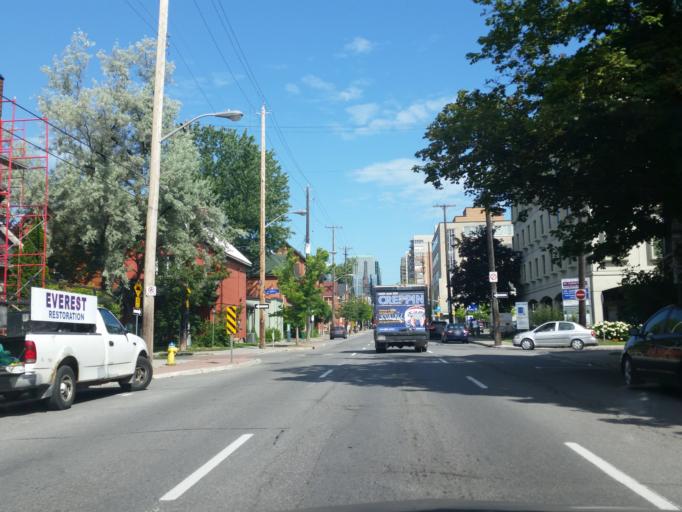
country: CA
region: Ontario
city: Ottawa
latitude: 45.4122
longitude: -75.6966
